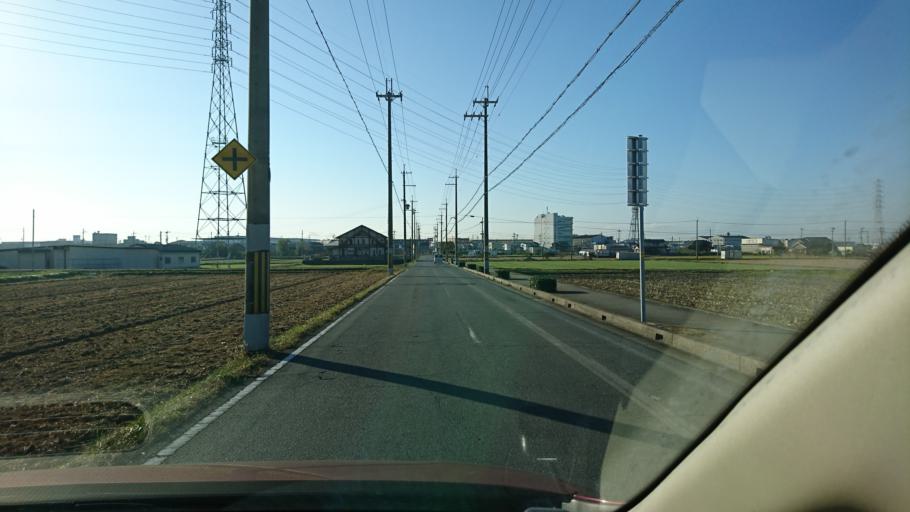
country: JP
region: Hyogo
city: Miki
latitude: 34.7367
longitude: 134.9222
